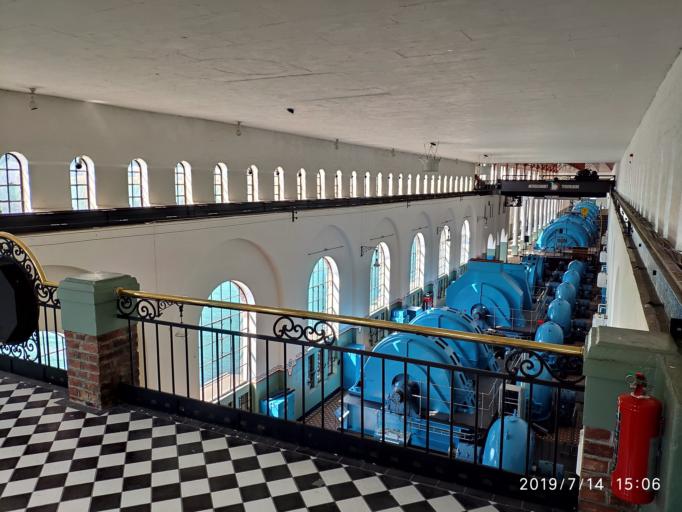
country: NO
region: Hordaland
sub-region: Odda
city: Odda
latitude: 60.1211
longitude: 6.5562
